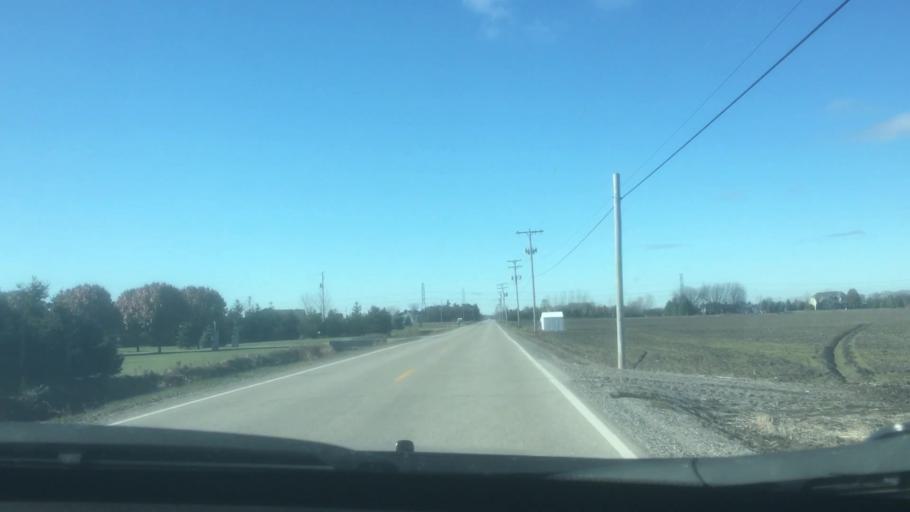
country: US
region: Michigan
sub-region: Bay County
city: Essexville
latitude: 43.5799
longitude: -83.7844
